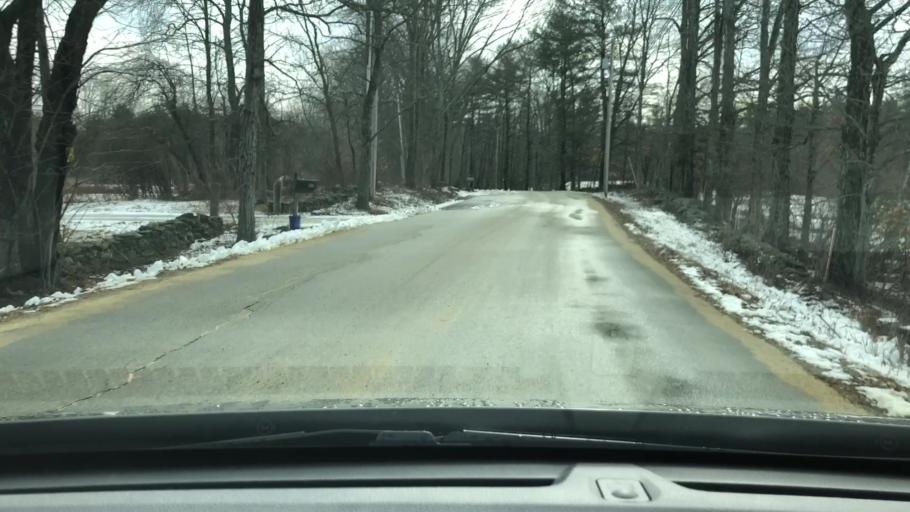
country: US
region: New Hampshire
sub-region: Strafford County
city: Madbury
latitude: 43.1847
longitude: -70.9746
